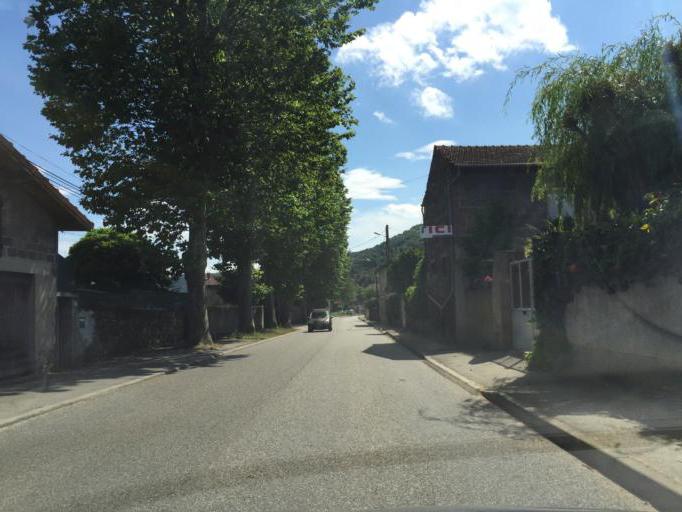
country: FR
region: Rhone-Alpes
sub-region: Departement de la Drome
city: Saint-Vallier
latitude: 45.1451
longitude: 4.8101
